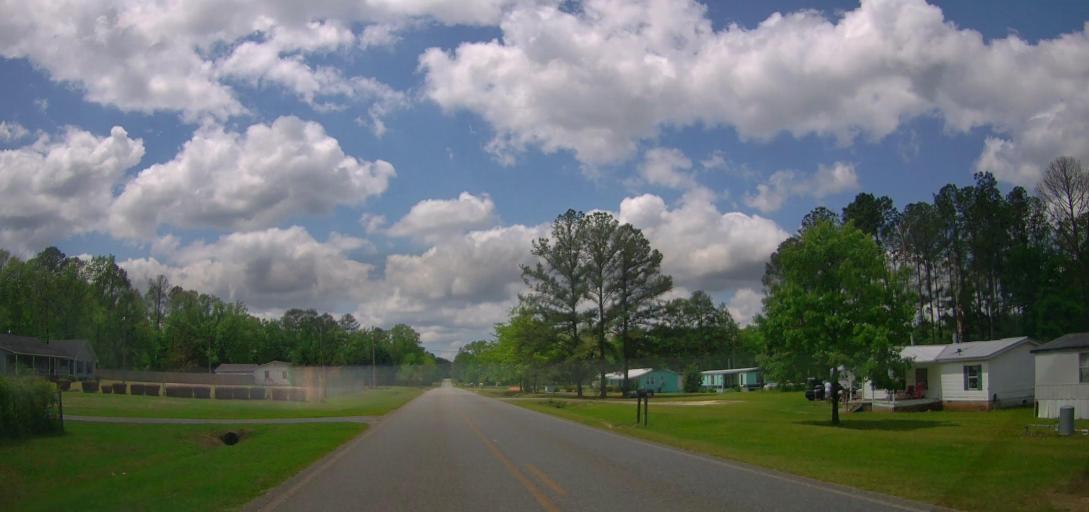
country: US
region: Georgia
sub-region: Laurens County
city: Dublin
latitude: 32.5974
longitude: -83.0152
